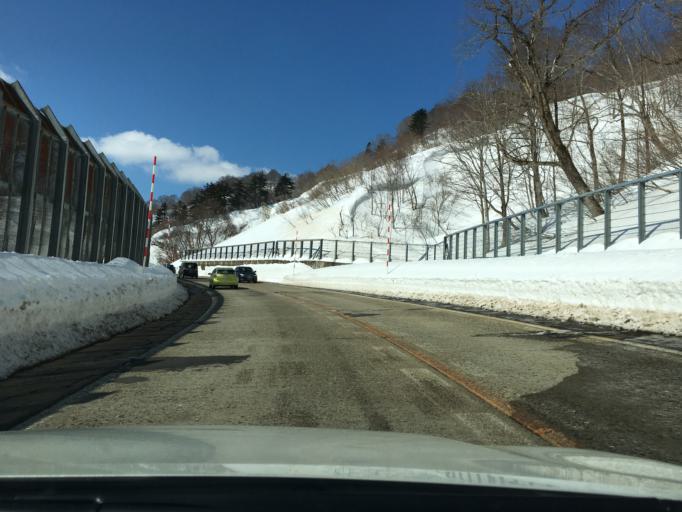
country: JP
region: Yamagata
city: Tsuruoka
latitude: 38.4911
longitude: 139.9841
